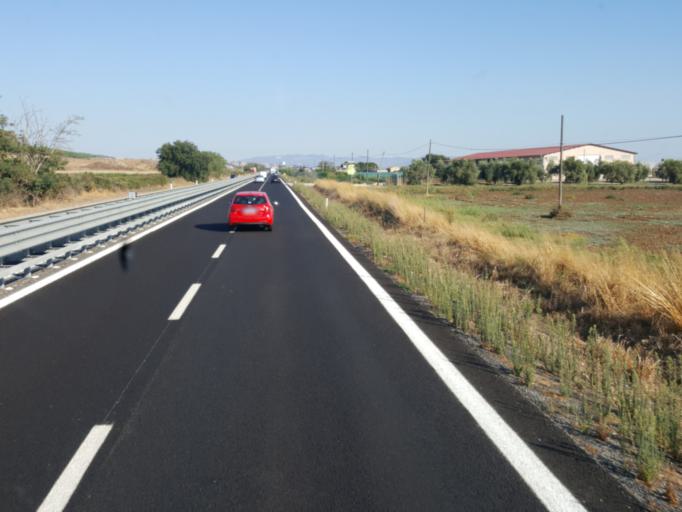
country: IT
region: Latium
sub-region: Provincia di Viterbo
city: Tarquinia
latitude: 42.2765
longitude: 11.7036
